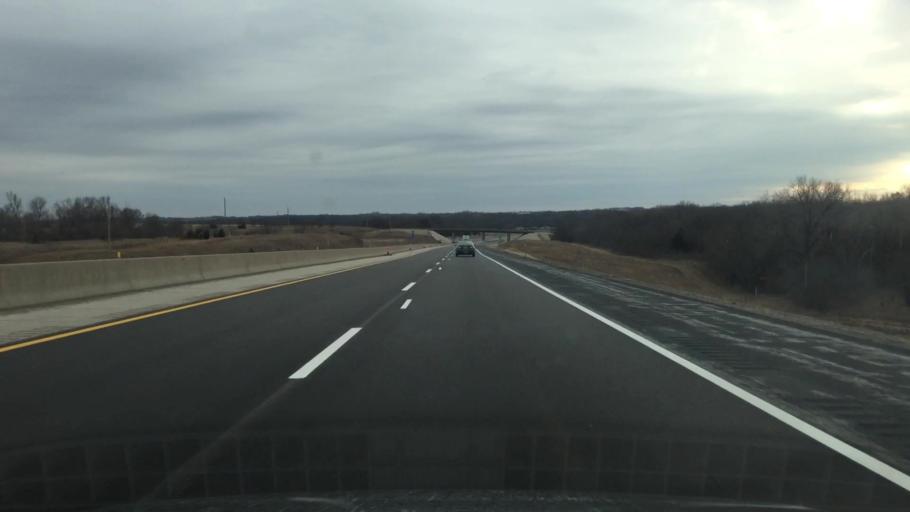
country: US
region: Kansas
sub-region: Osage County
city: Osage City
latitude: 38.6273
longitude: -96.0449
